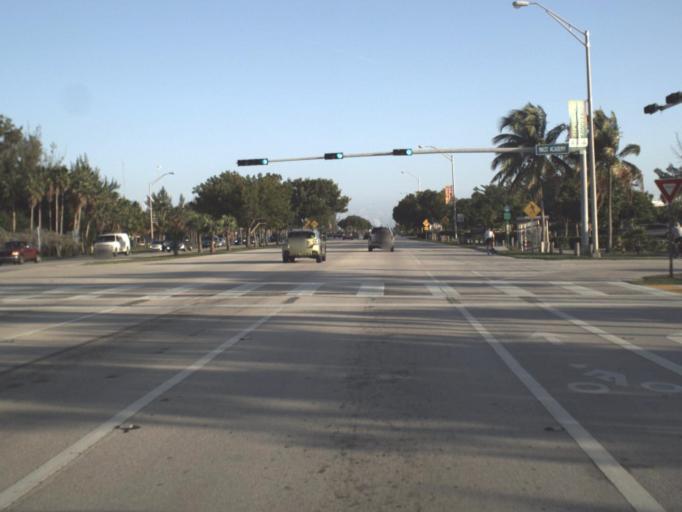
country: US
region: Florida
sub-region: Miami-Dade County
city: Key Biscayne
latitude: 25.7380
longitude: -80.1673
